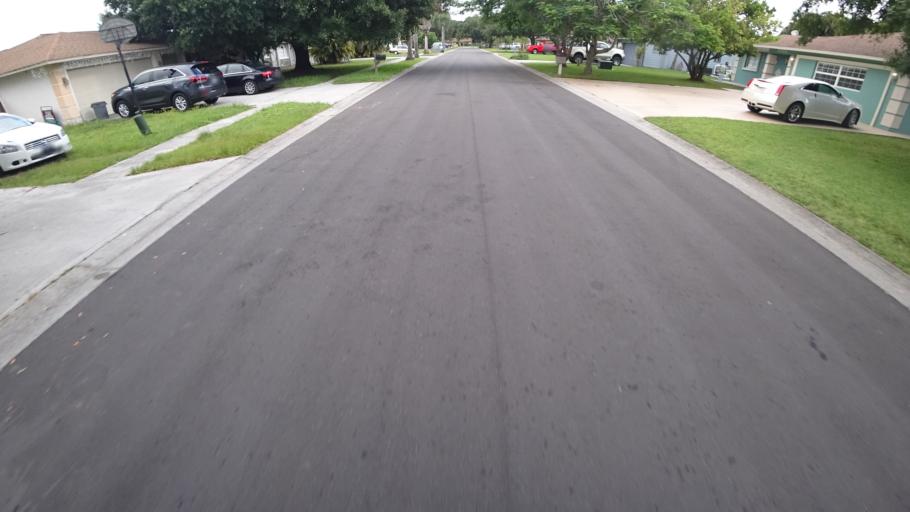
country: US
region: Florida
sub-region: Manatee County
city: Whitfield
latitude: 27.4143
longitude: -82.5493
